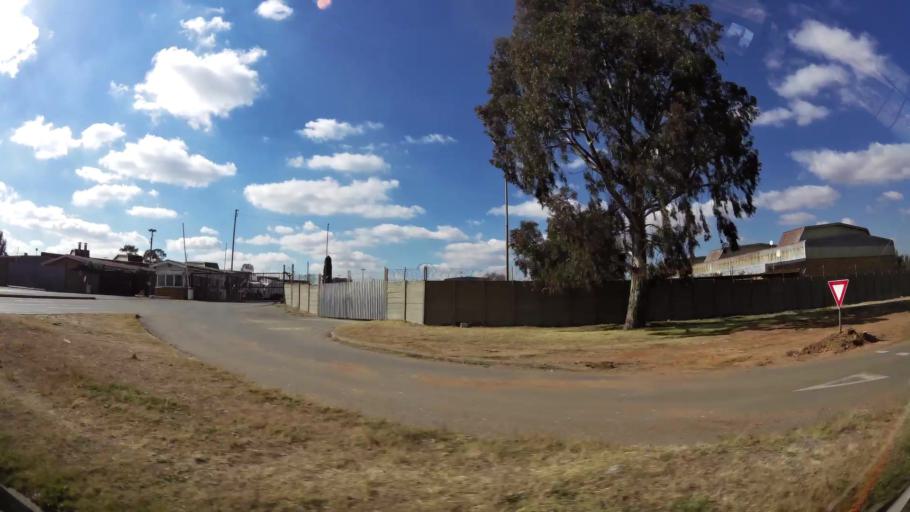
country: ZA
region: Gauteng
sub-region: West Rand District Municipality
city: Krugersdorp
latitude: -26.1283
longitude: 27.8021
